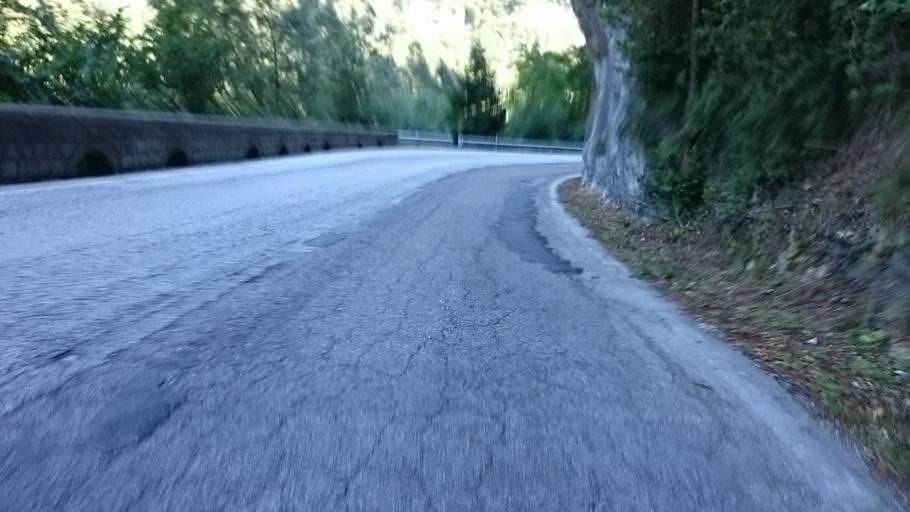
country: IT
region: Veneto
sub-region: Provincia di Belluno
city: Ospitale di Cadore
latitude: 46.3141
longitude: 12.3220
